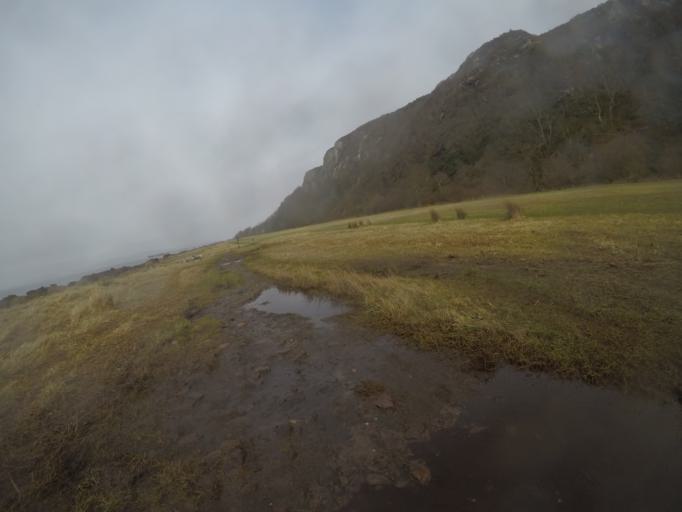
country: GB
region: Scotland
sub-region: North Ayrshire
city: Millport
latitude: 55.7083
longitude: -4.9042
